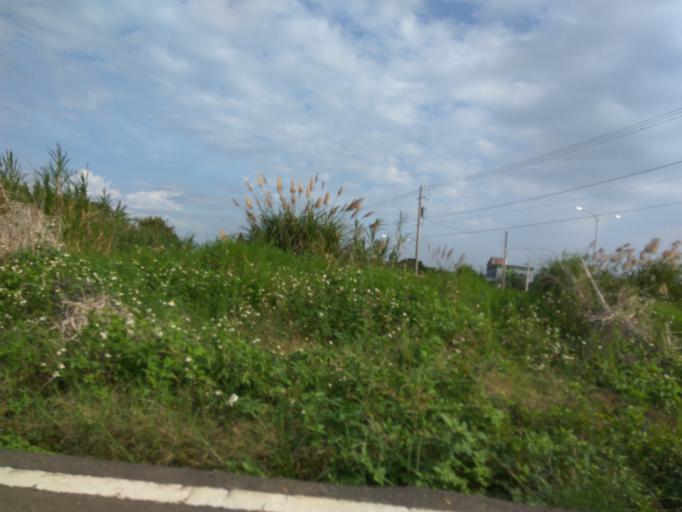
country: TW
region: Taiwan
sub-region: Hsinchu
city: Zhubei
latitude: 24.9628
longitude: 121.0142
